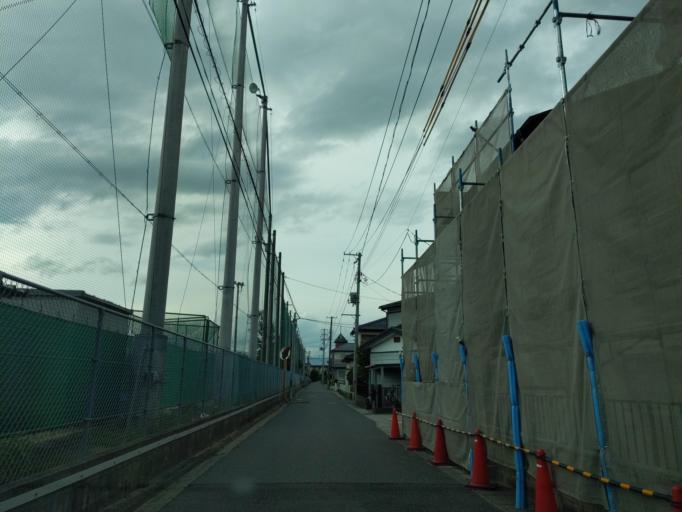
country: JP
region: Fukushima
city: Koriyama
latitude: 37.4020
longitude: 140.3394
